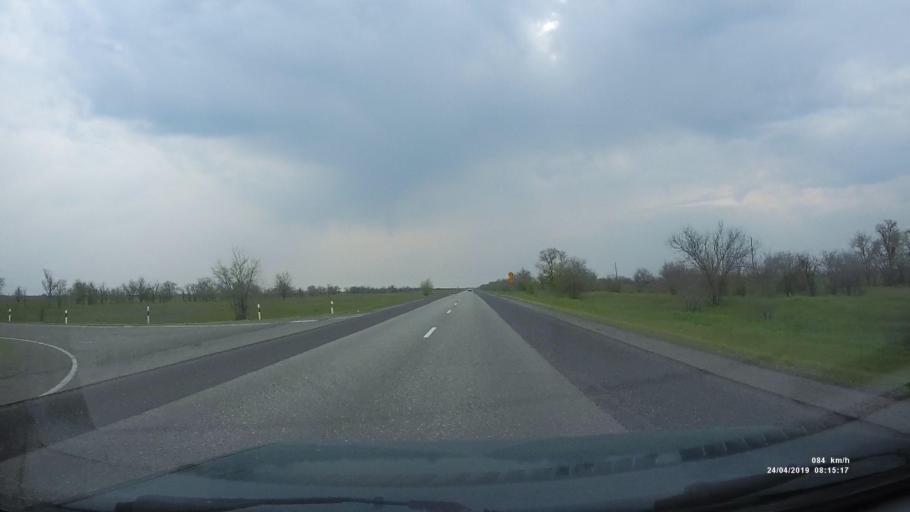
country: RU
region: Kalmykiya
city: Priyutnoye
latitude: 46.1002
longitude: 43.5915
